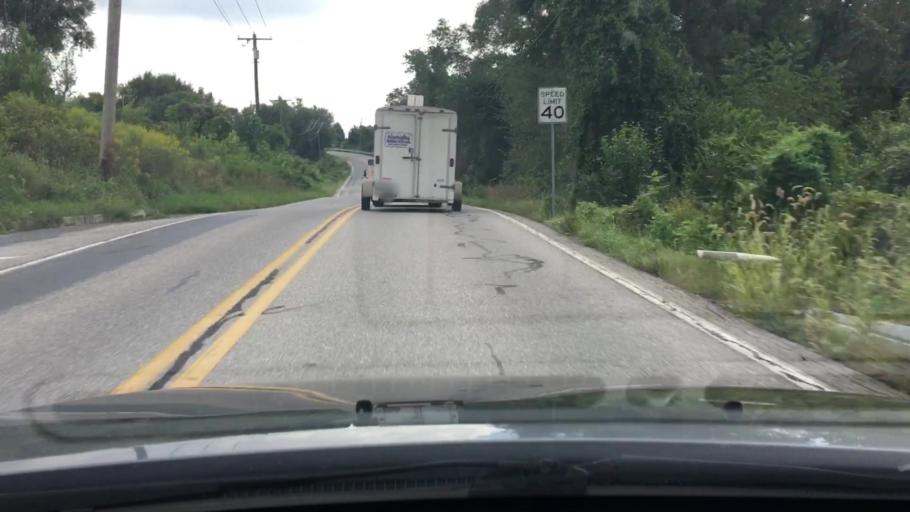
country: US
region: Pennsylvania
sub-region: Franklin County
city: Scotland
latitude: 39.9557
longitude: -77.5838
